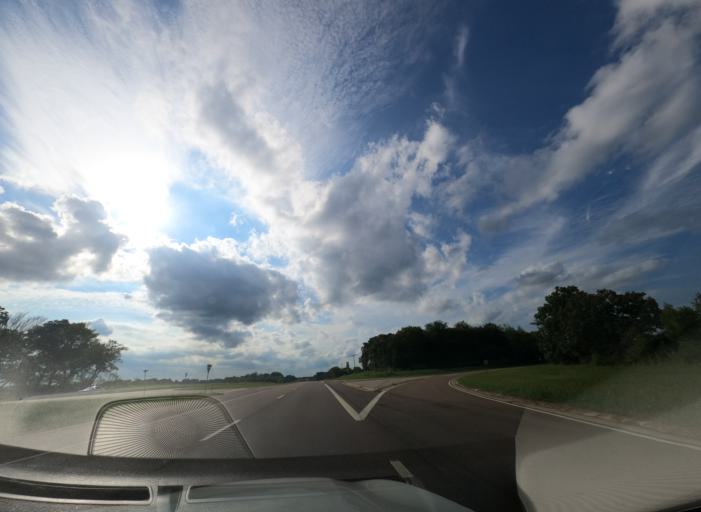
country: US
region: Tennessee
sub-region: Fayette County
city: Piperton
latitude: 34.9775
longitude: -89.5732
